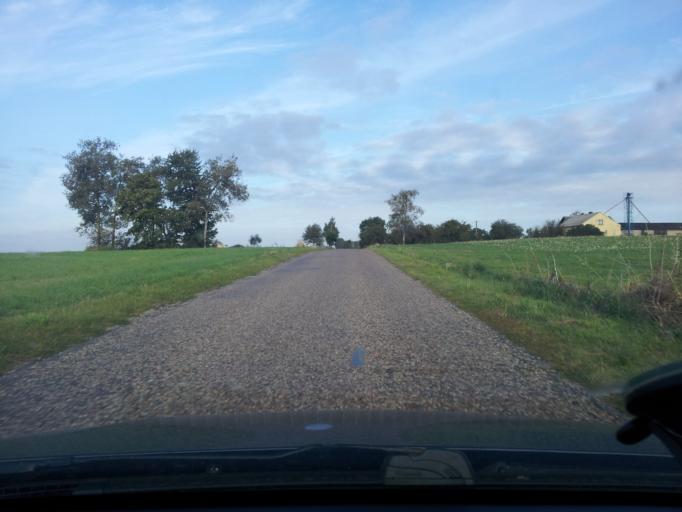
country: PL
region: Kujawsko-Pomorskie
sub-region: Powiat brodnicki
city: Bartniczka
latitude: 53.2052
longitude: 19.5927
